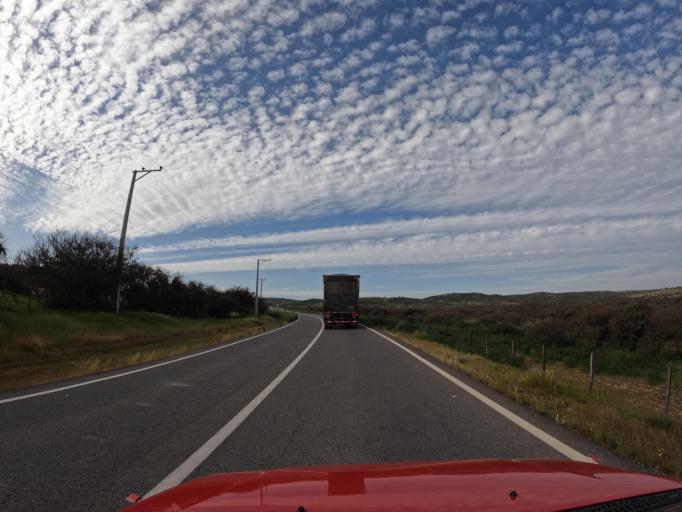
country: CL
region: O'Higgins
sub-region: Provincia de Colchagua
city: Santa Cruz
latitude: -34.3276
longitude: -71.7442
